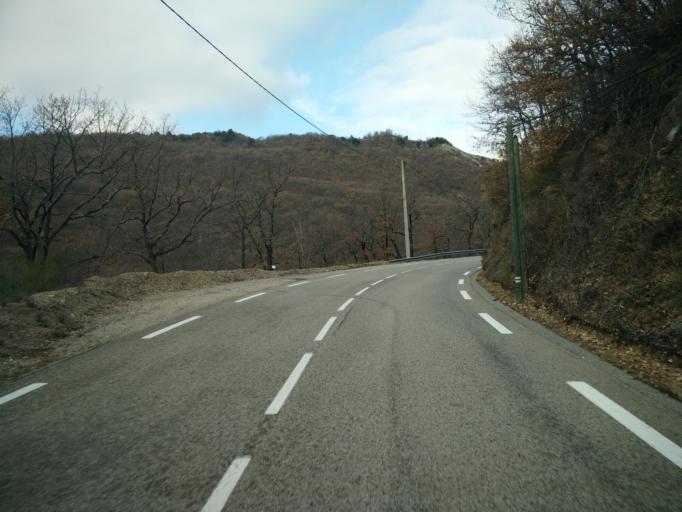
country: FR
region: Provence-Alpes-Cote d'Azur
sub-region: Departement des Alpes-Maritimes
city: Tourrettes-sur-Loup
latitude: 43.7777
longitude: 6.9791
